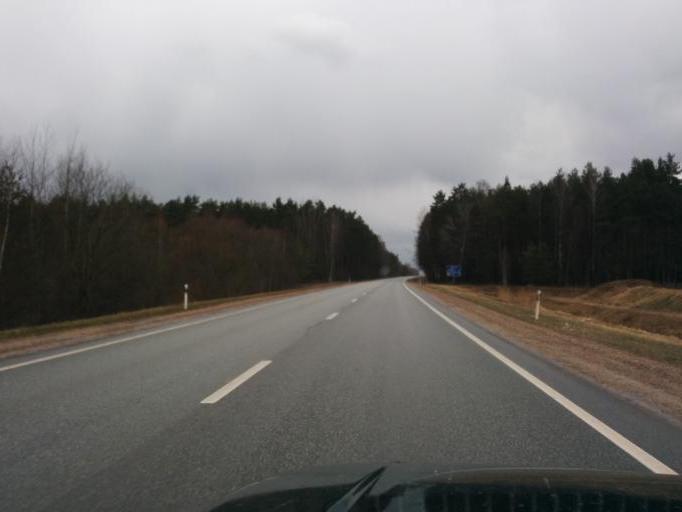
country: LV
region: Marupe
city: Marupe
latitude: 56.8412
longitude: 24.0234
